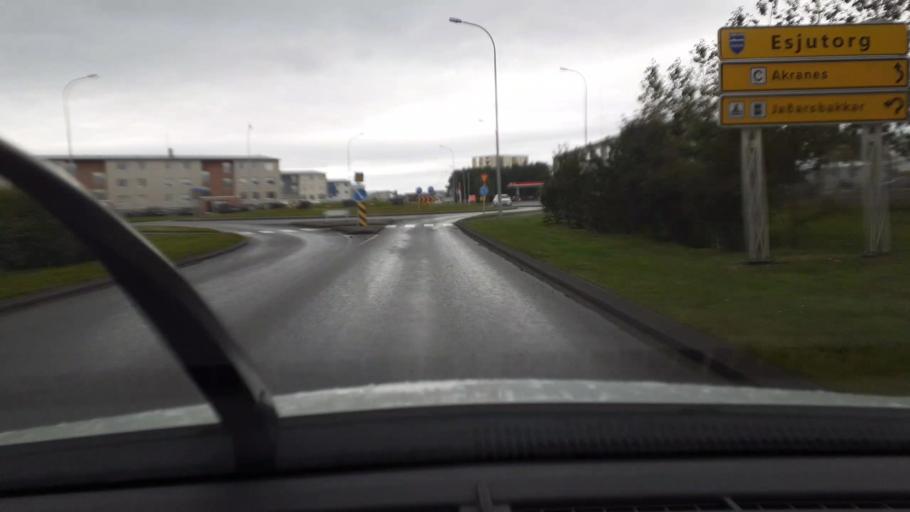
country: IS
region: West
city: Akranes
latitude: 64.3231
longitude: -22.0615
